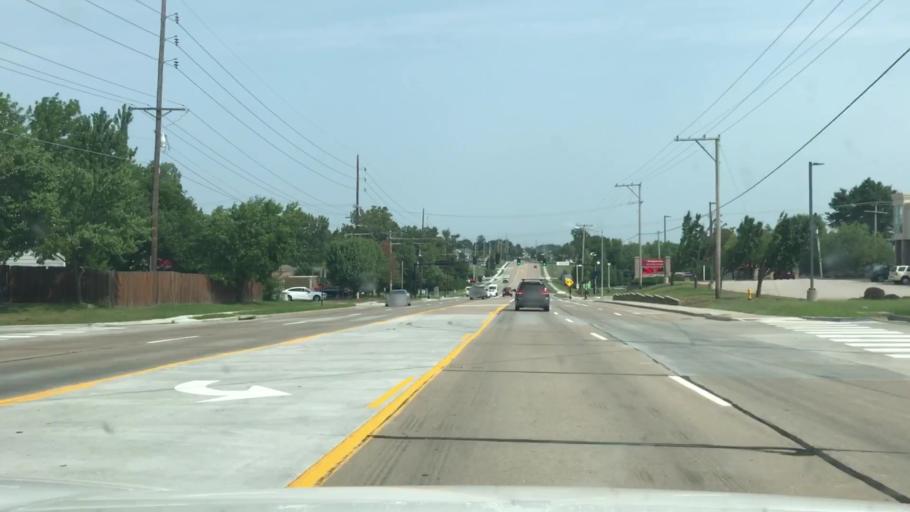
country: US
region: Missouri
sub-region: Saint Charles County
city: Dardenne Prairie
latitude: 38.7868
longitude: -90.7369
